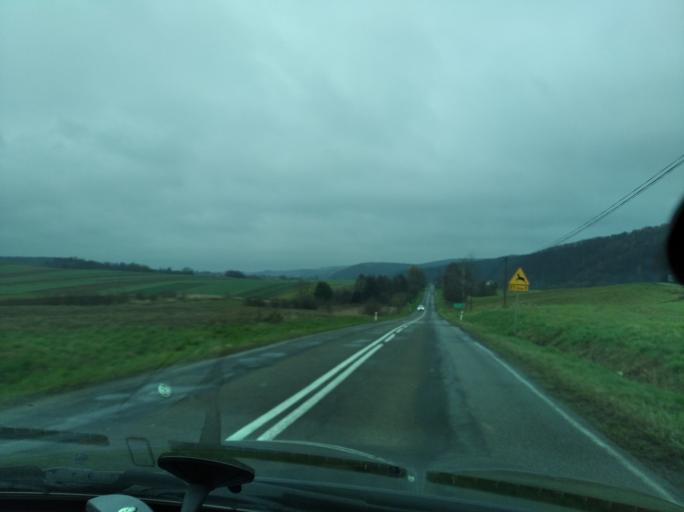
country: PL
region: Subcarpathian Voivodeship
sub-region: Powiat rzeszowski
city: Dynow
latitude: 49.8466
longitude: 22.2441
